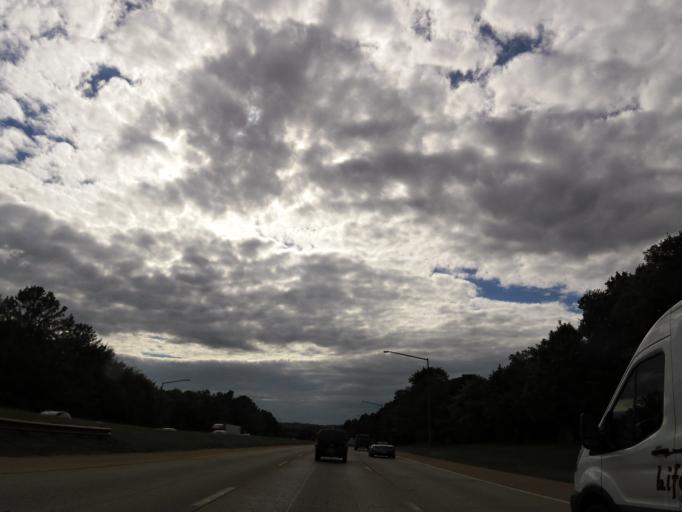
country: US
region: Tennessee
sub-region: Davidson County
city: Oak Hill
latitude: 36.1217
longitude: -86.7574
